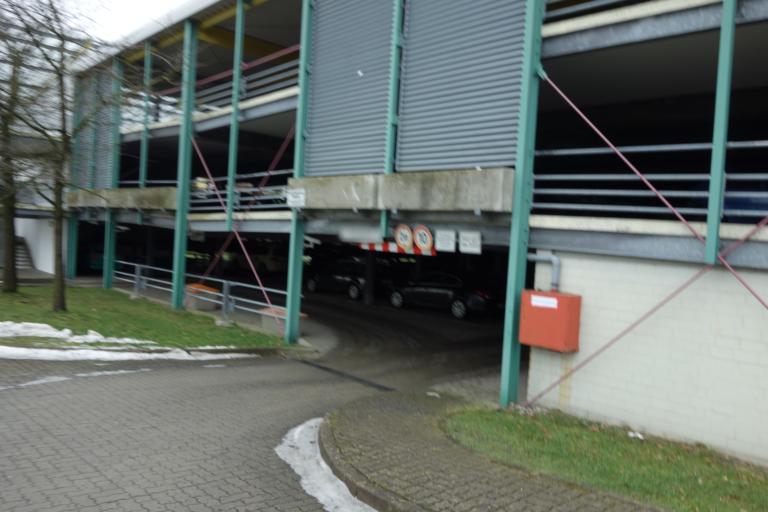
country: DE
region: Saxony
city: Freiberg
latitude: 50.9202
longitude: 13.3211
